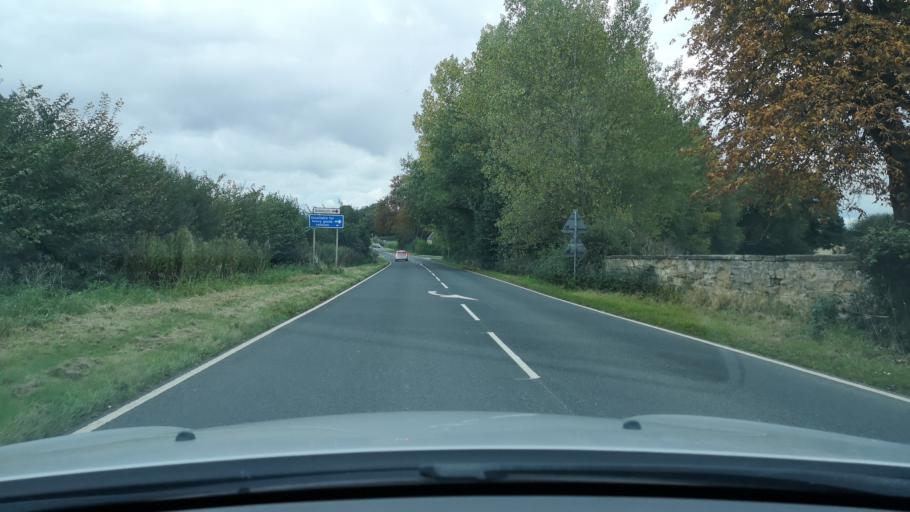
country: GB
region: England
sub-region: City and Borough of Wakefield
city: Low Ackworth
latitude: 53.6597
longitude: -1.3030
